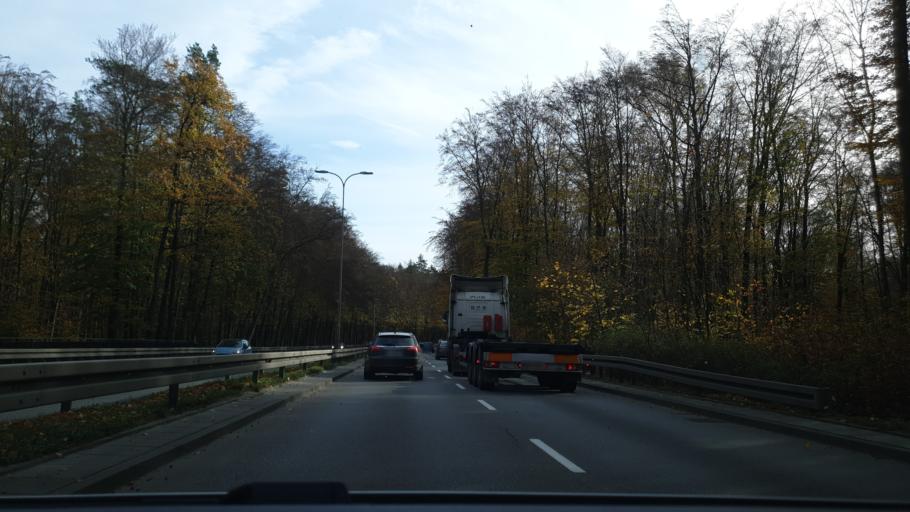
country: PL
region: Pomeranian Voivodeship
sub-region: Powiat gdanski
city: Kowale
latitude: 54.3753
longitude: 18.5369
